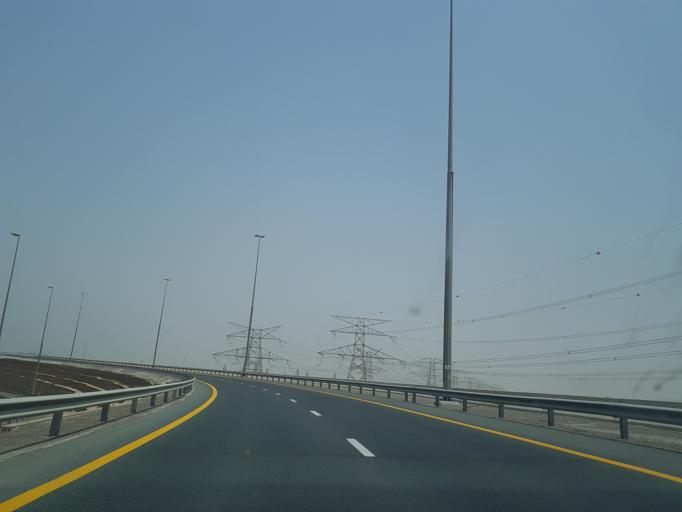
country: AE
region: Dubai
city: Dubai
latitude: 25.0858
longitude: 55.3944
